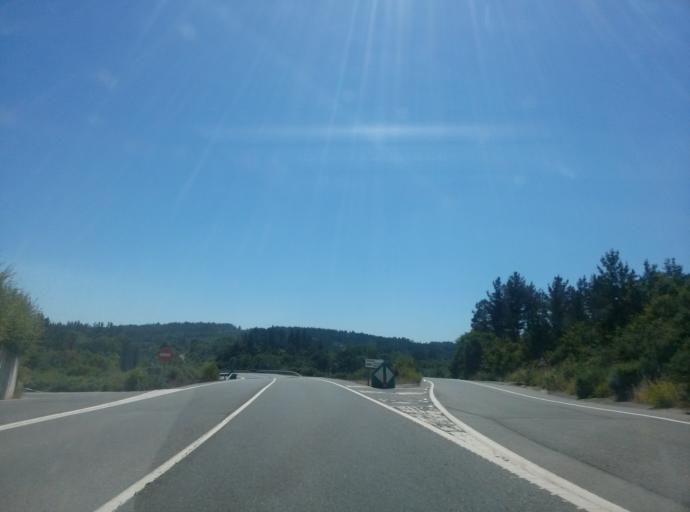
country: ES
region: Galicia
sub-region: Provincia de Lugo
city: Mos
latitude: 43.0997
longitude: -7.4732
